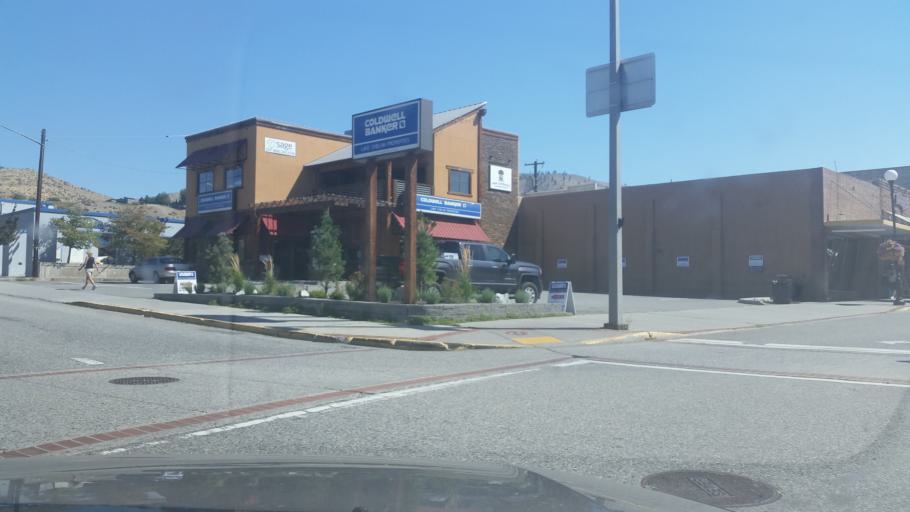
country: US
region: Washington
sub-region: Chelan County
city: Chelan
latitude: 47.8400
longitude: -120.0194
